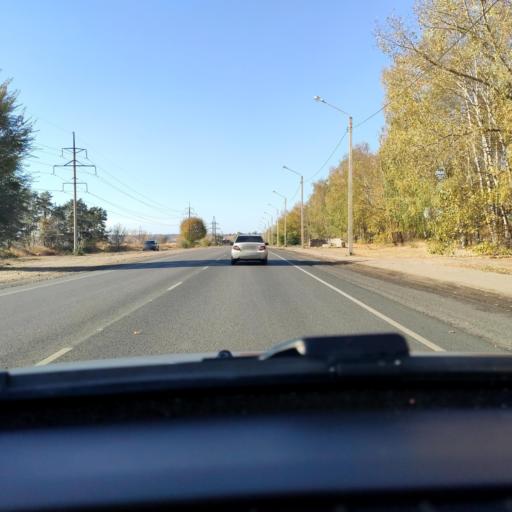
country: RU
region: Voronezj
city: Pridonskoy
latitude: 51.6971
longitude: 39.0849
